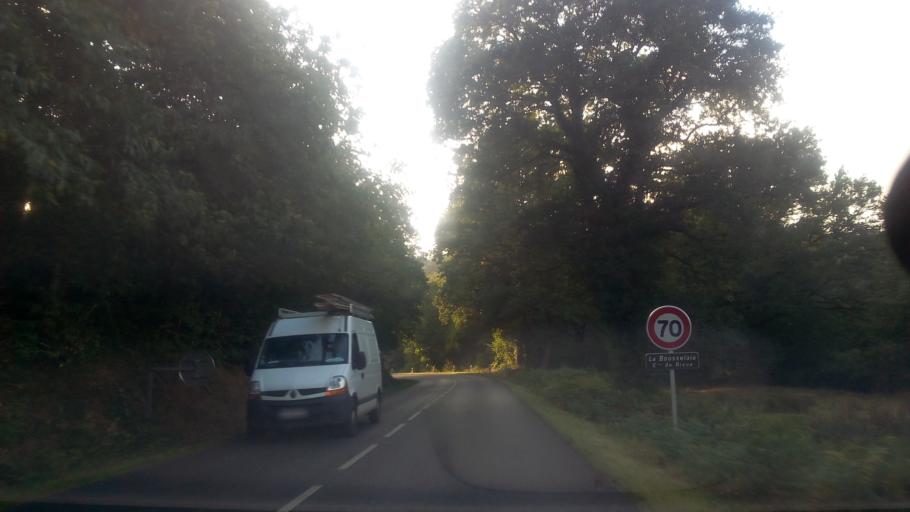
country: FR
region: Brittany
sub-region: Departement du Morbihan
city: Saint-Jean-la-Poterie
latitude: 47.6254
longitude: -2.1247
